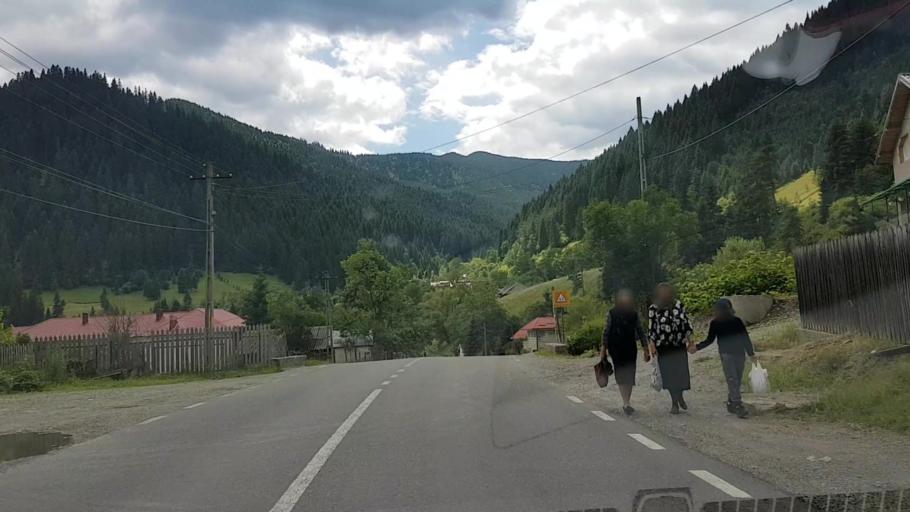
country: RO
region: Neamt
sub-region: Comuna Borca
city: Borca
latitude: 47.2054
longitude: 25.7515
